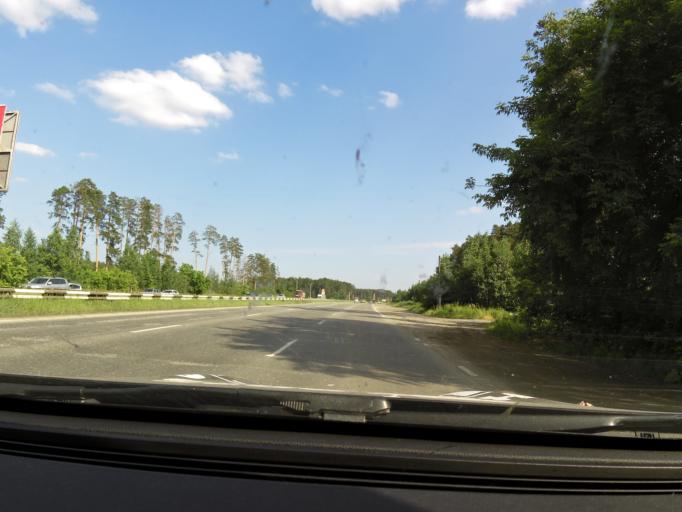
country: RU
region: Sverdlovsk
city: Shirokaya Rechka
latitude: 56.8206
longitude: 60.5027
